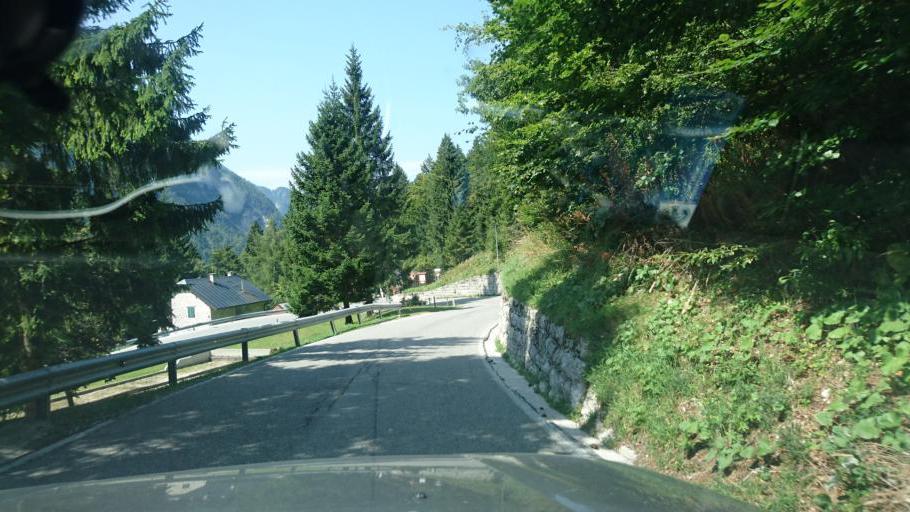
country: SI
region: Bovec
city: Bovec
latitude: 46.3913
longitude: 13.4729
